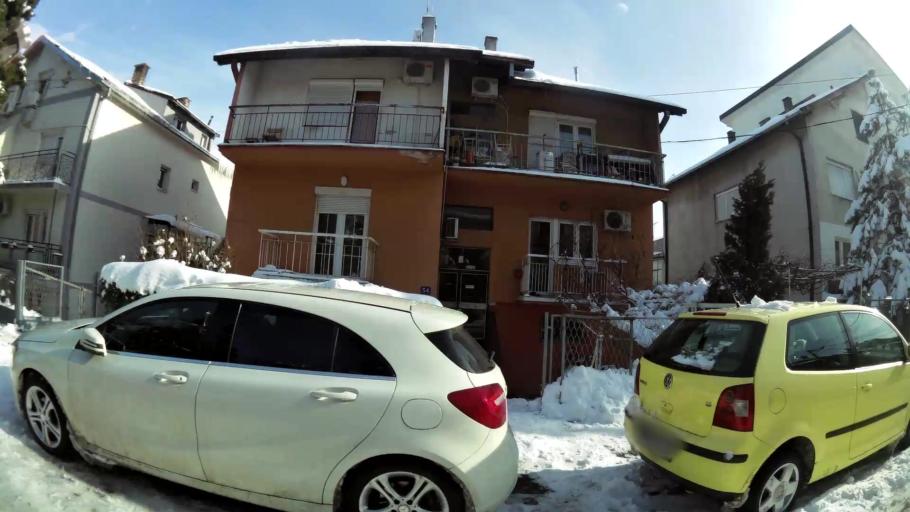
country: RS
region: Central Serbia
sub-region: Belgrade
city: Palilula
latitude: 44.7975
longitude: 20.5251
